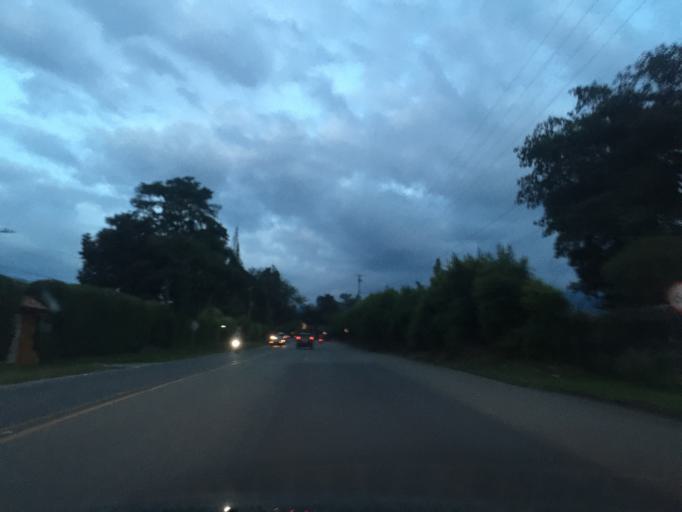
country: CO
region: Quindio
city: Armenia
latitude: 4.5004
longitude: -75.7236
